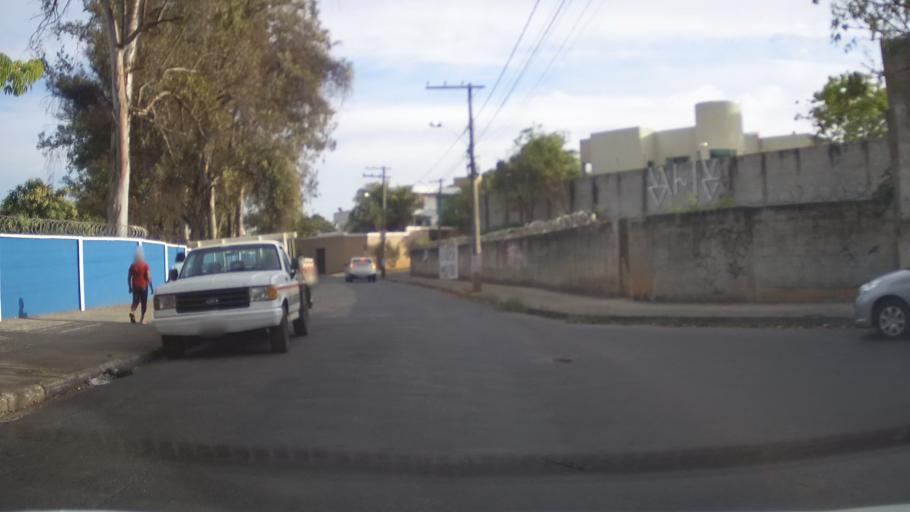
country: BR
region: Minas Gerais
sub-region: Belo Horizonte
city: Belo Horizonte
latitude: -19.8651
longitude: -43.9959
